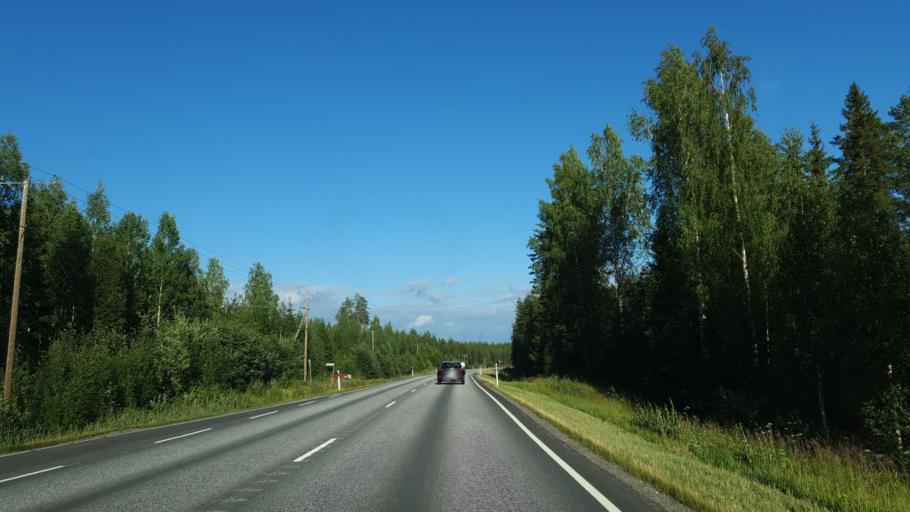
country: FI
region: North Karelia
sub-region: Joensuu
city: Outokumpu
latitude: 62.5324
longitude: 28.9688
